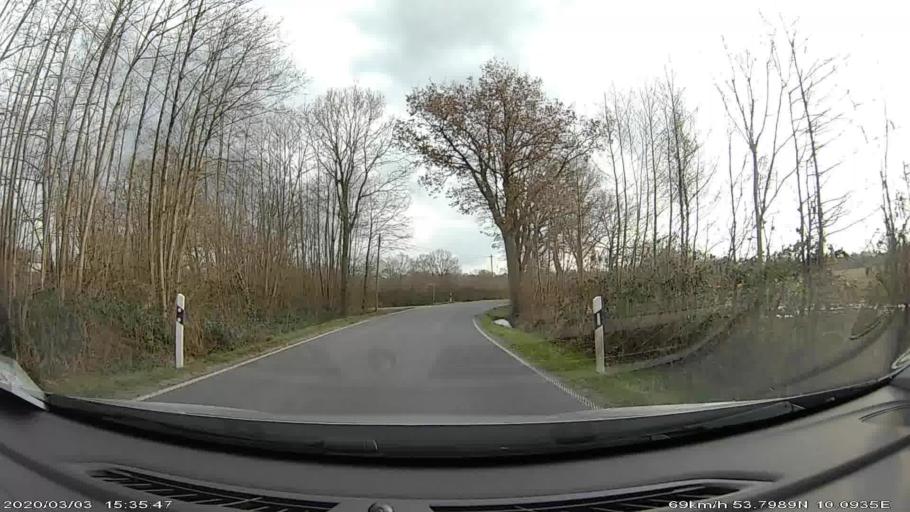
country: DE
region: Schleswig-Holstein
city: Nahe
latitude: 53.7998
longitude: 10.0930
